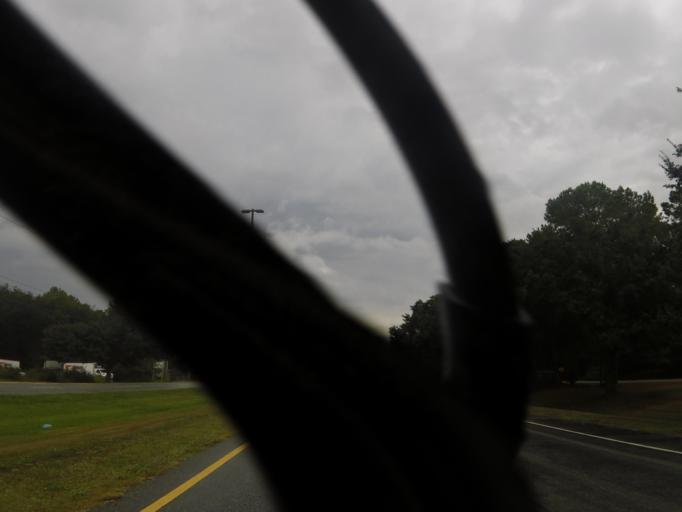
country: US
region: Alabama
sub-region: Baldwin County
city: Daphne
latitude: 30.5777
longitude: -87.8981
